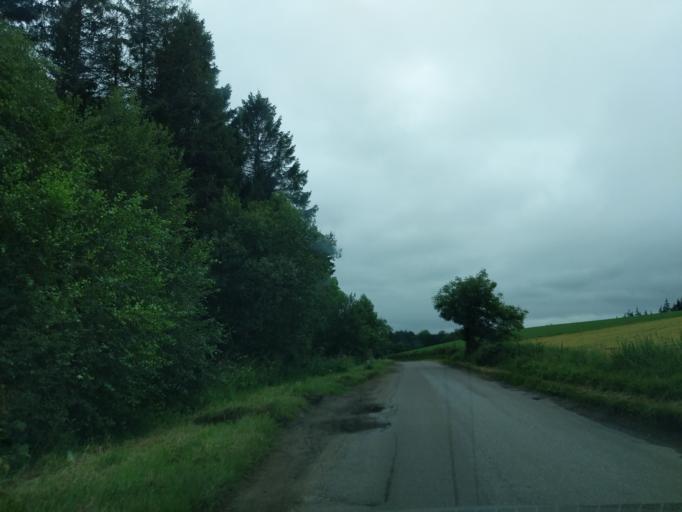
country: GB
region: Scotland
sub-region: Moray
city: Rothes
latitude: 57.4781
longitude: -3.1901
